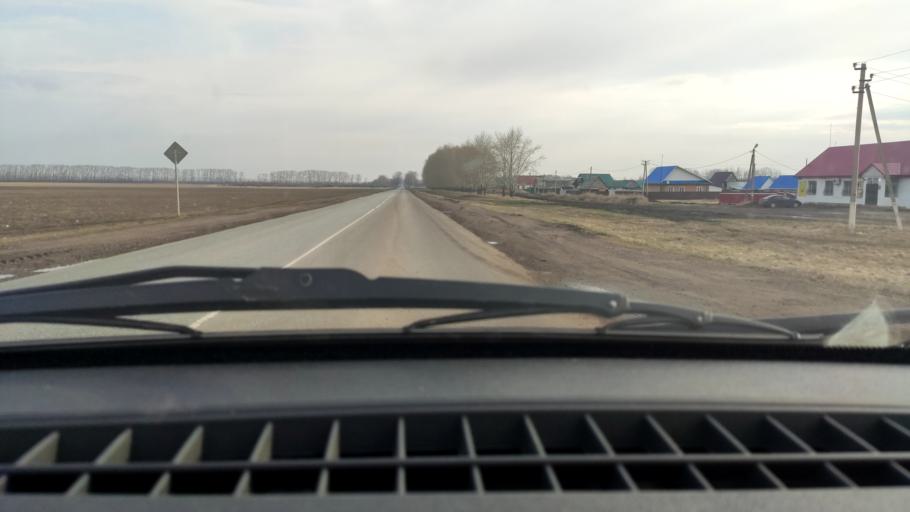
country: RU
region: Bashkortostan
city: Davlekanovo
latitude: 54.3928
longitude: 55.2050
